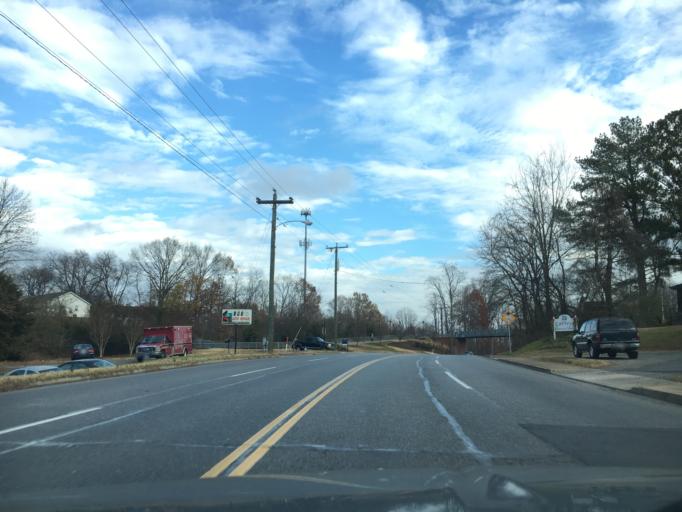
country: US
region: Virginia
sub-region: Prince Edward County
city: Farmville
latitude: 37.3043
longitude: -78.4015
